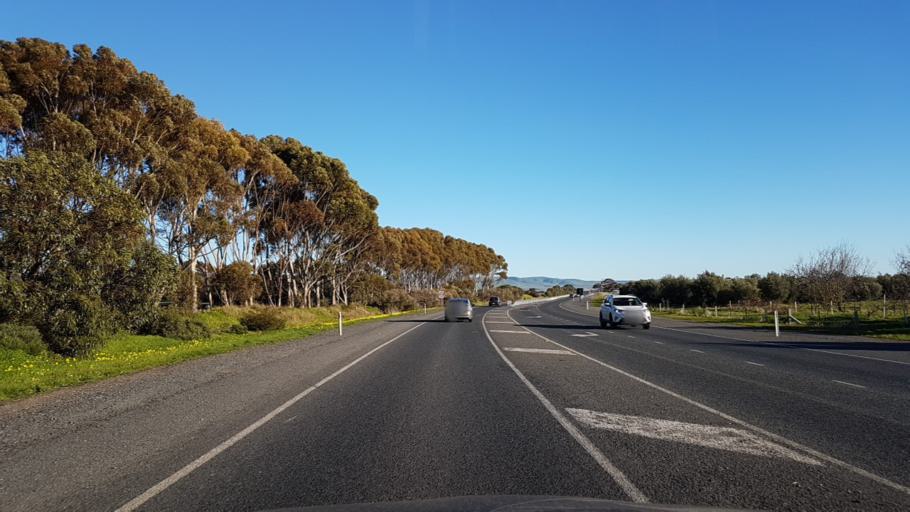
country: AU
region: South Australia
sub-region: Onkaparinga
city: Aldinga
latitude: -35.2541
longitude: 138.4944
